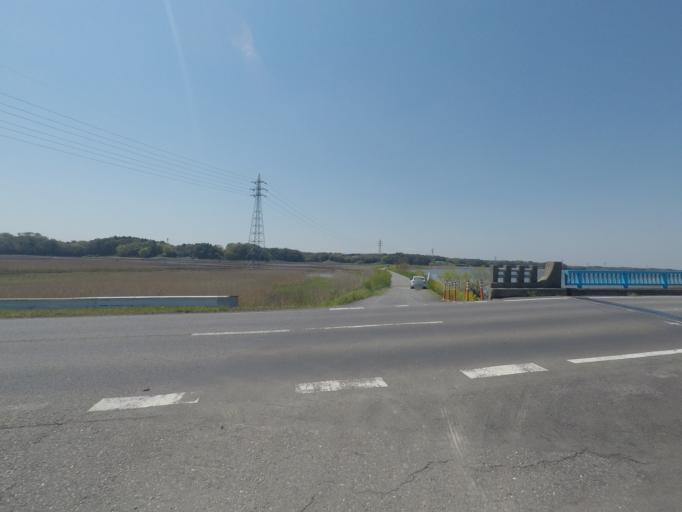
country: JP
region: Ibaraki
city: Ushiku
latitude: 35.9536
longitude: 140.1030
